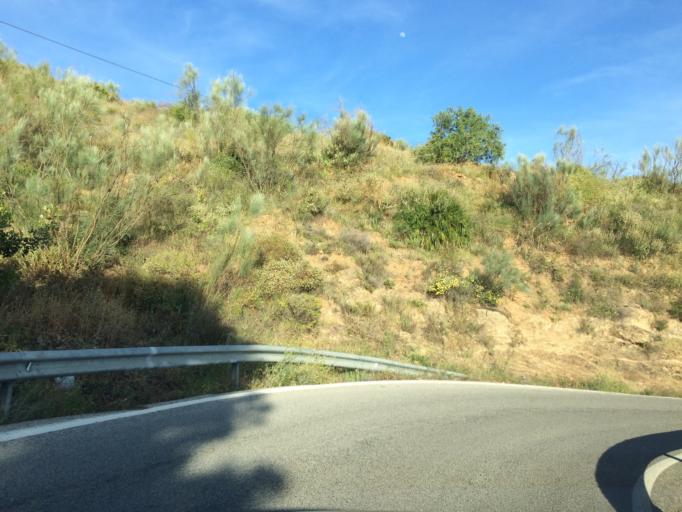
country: ES
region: Andalusia
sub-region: Provincia de Malaga
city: Totalan
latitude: 36.7456
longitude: -4.3302
